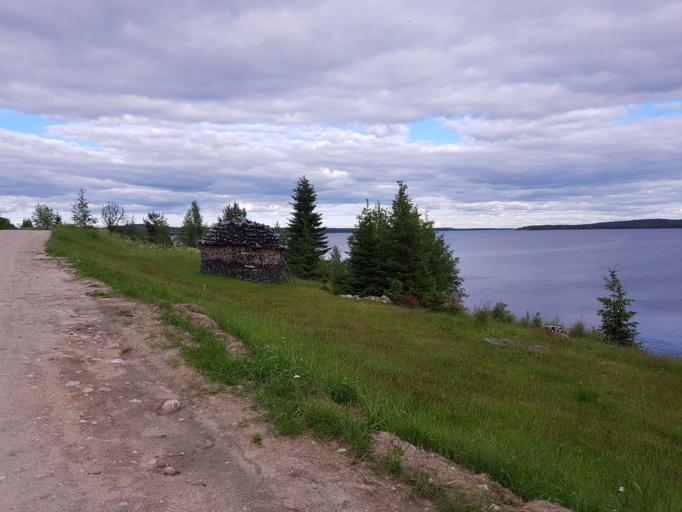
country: RU
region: Republic of Karelia
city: Kalevala
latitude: 65.1915
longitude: 31.1657
